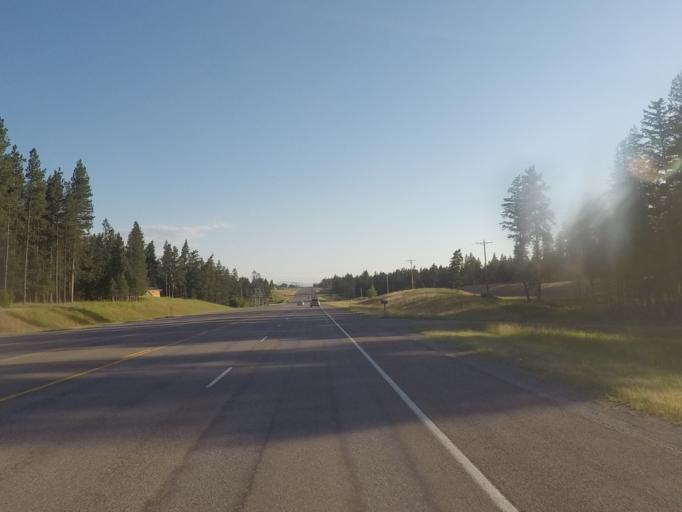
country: US
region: Montana
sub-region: Flathead County
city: Columbia Falls
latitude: 48.3762
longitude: -114.1311
